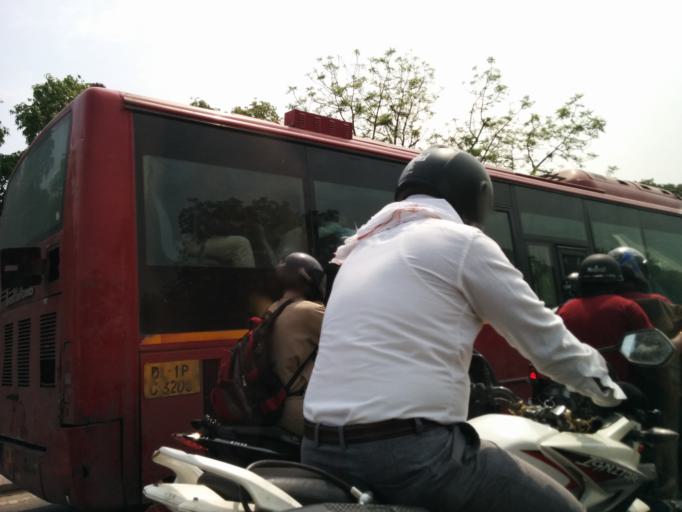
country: IN
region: NCT
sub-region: New Delhi
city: New Delhi
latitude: 28.5444
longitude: 77.2022
